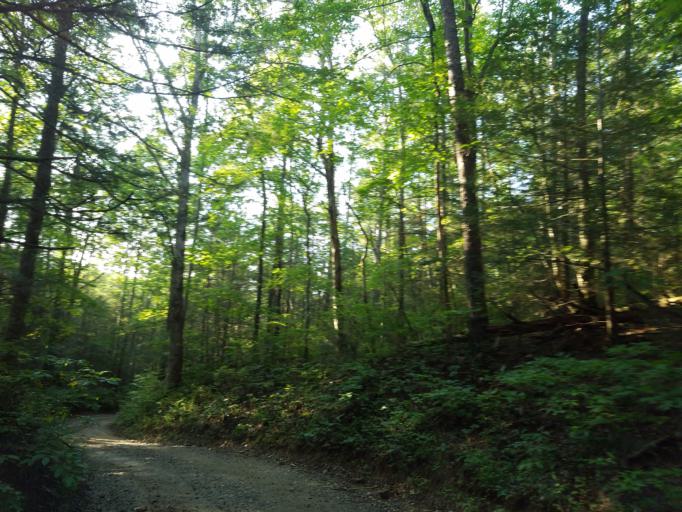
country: US
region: Georgia
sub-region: Lumpkin County
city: Dahlonega
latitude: 34.6562
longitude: -84.0853
